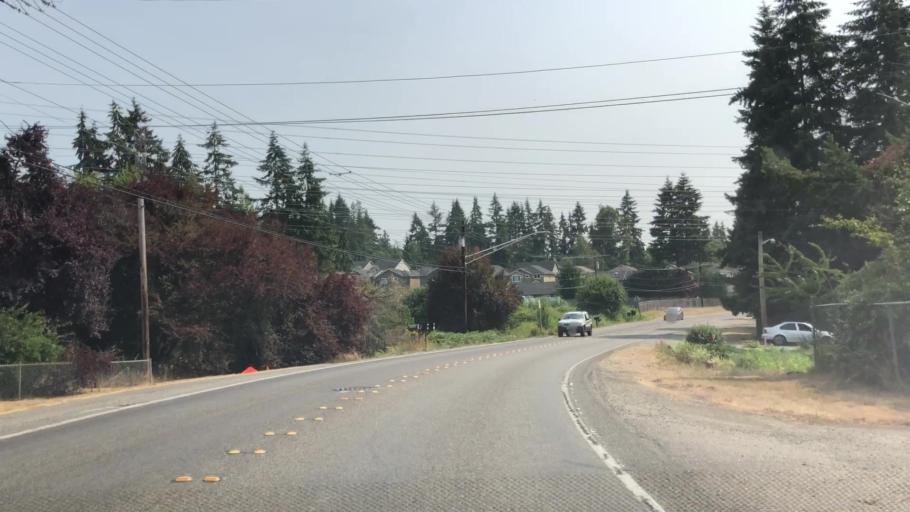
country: US
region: Washington
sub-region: Snohomish County
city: Brier
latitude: 47.8046
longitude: -122.2529
